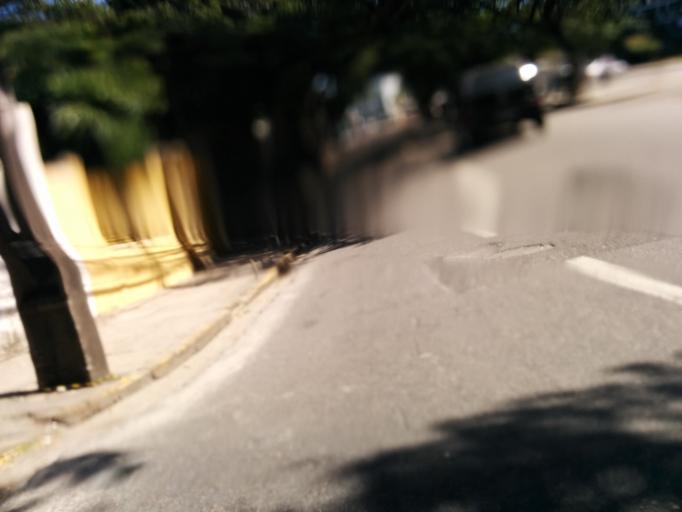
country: BR
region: Pernambuco
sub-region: Recife
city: Recife
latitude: -8.0533
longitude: -34.8900
